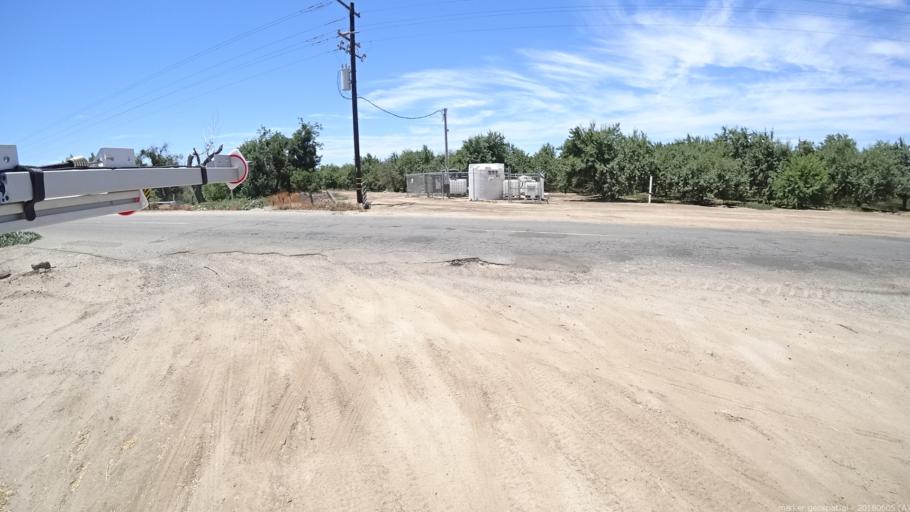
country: US
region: California
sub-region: Madera County
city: Chowchilla
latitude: 37.1412
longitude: -120.3109
